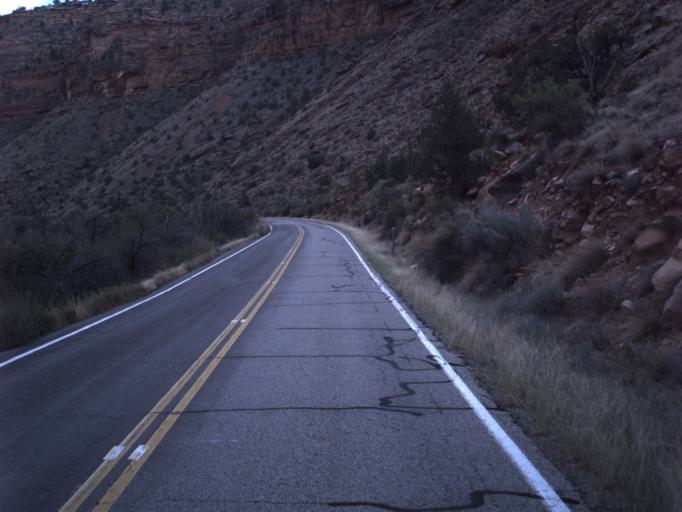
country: US
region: Utah
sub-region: Grand County
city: Moab
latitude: 38.7978
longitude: -109.3318
